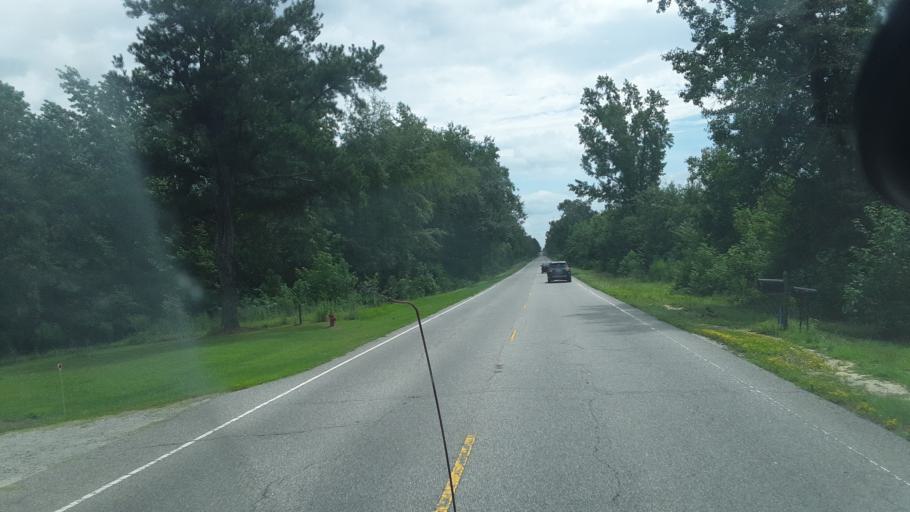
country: US
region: North Carolina
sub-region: Robeson County
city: Maxton
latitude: 34.6556
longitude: -79.3789
